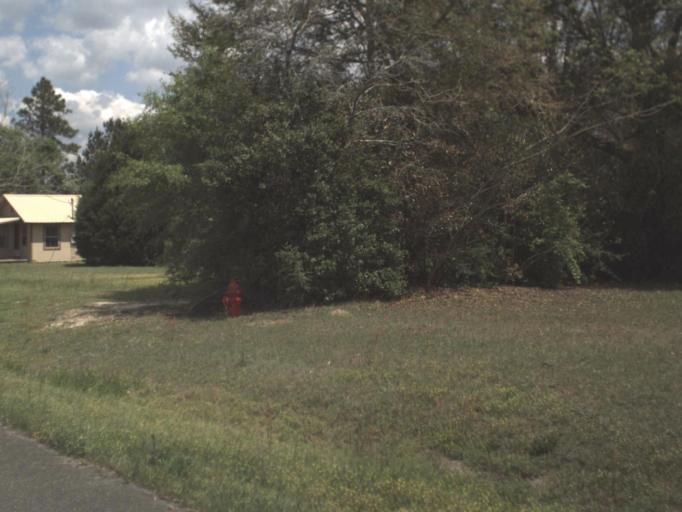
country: US
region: Florida
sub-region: Okaloosa County
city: Crestview
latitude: 30.8445
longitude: -86.6751
